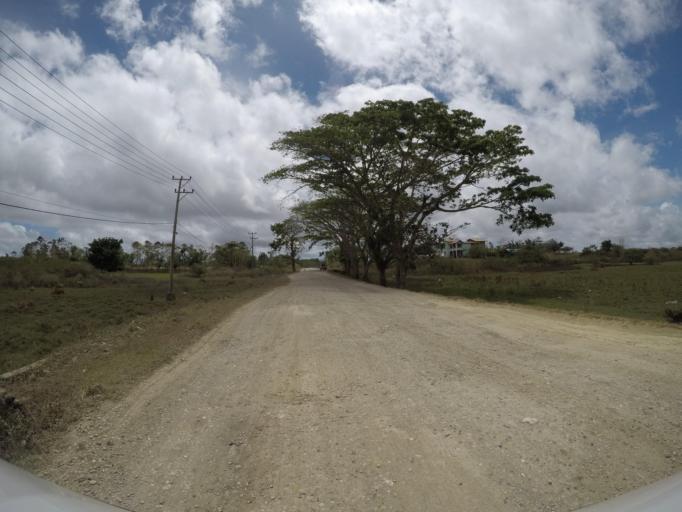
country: TL
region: Lautem
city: Lospalos
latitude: -8.4531
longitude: 127.0020
